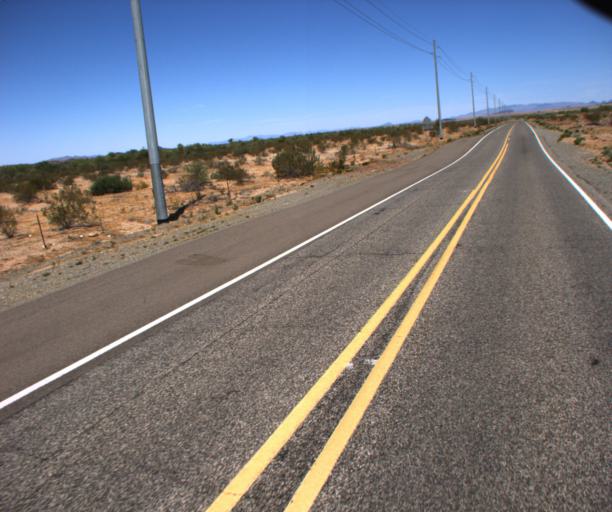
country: US
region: Arizona
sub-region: La Paz County
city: Cienega Springs
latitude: 33.9631
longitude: -114.0342
